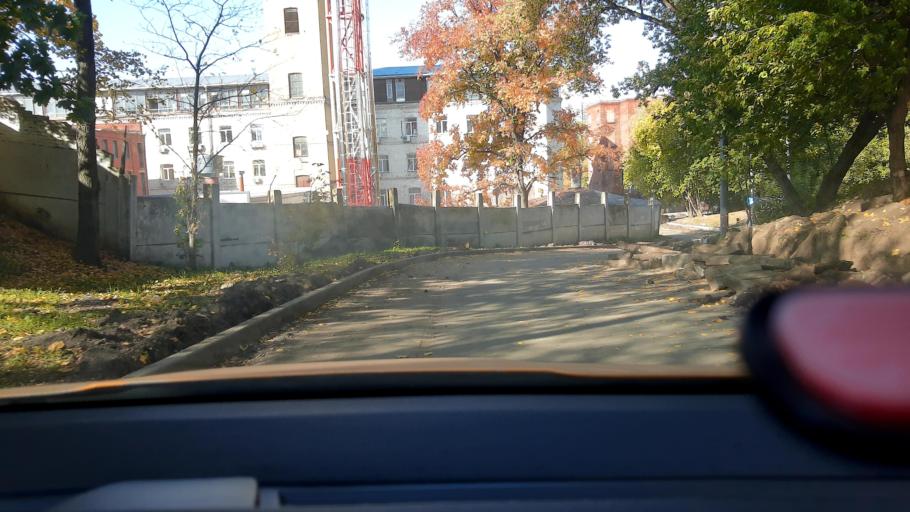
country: RU
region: Moscow
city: Strogino
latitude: 55.8383
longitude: 37.4135
